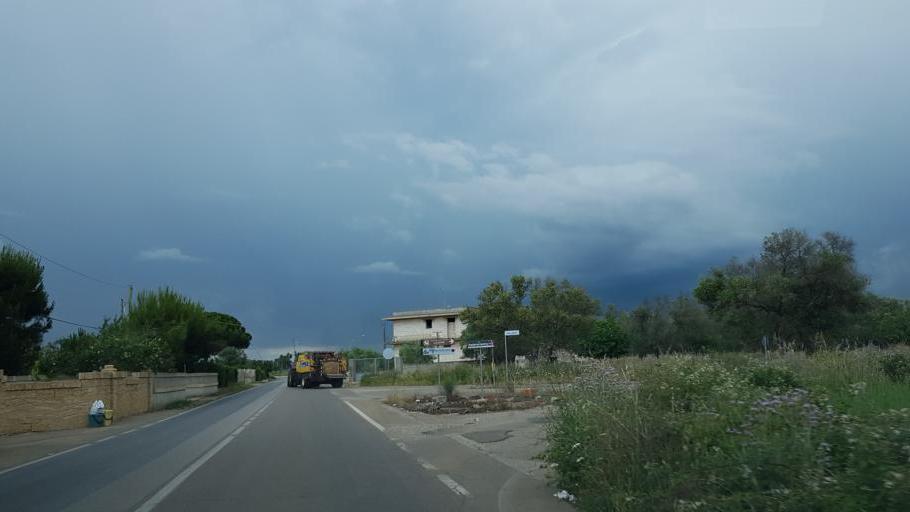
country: IT
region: Apulia
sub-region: Provincia di Lecce
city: Porto Cesareo
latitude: 40.3011
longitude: 17.8589
